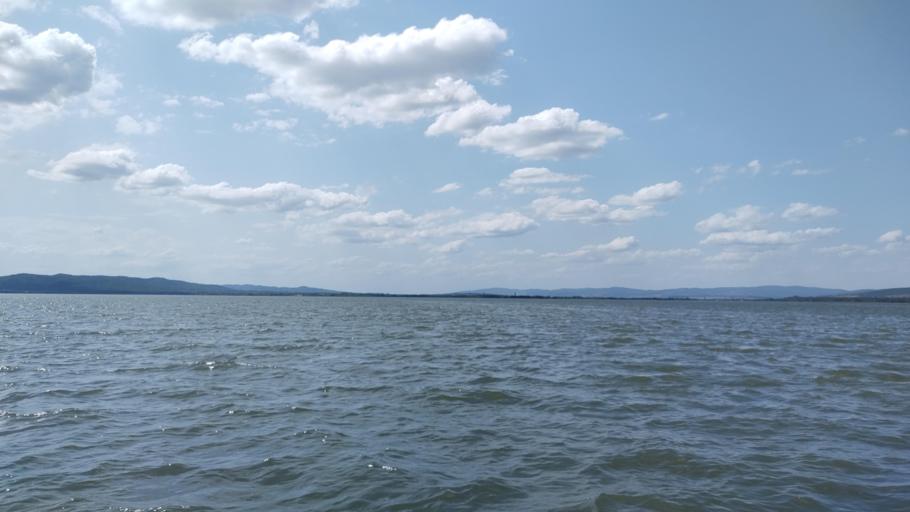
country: RO
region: Caras-Severin
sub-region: Comuna Pescari
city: Coronini
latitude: 44.6686
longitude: 21.6774
